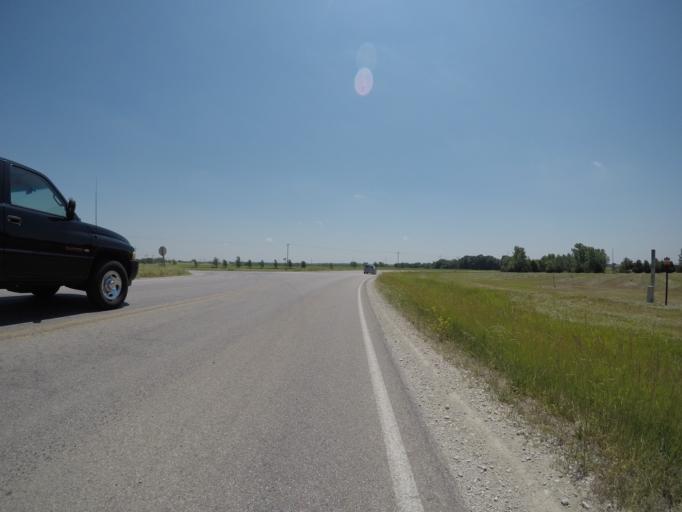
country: US
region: Kansas
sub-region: Riley County
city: Manhattan
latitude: 39.2322
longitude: -96.4421
